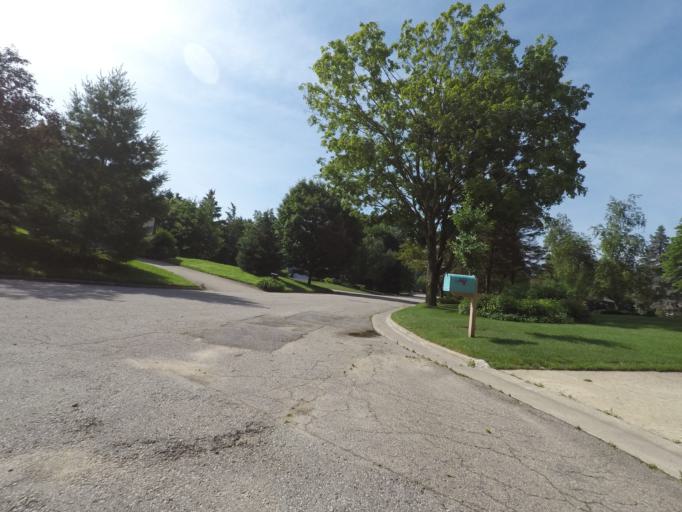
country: US
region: Wisconsin
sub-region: Dane County
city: Middleton
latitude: 43.0768
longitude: -89.4913
